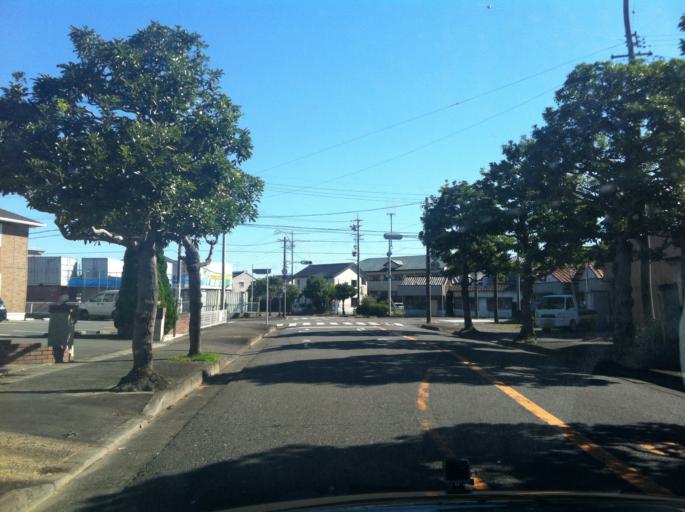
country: JP
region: Shizuoka
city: Shizuoka-shi
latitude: 34.9492
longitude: 138.4217
